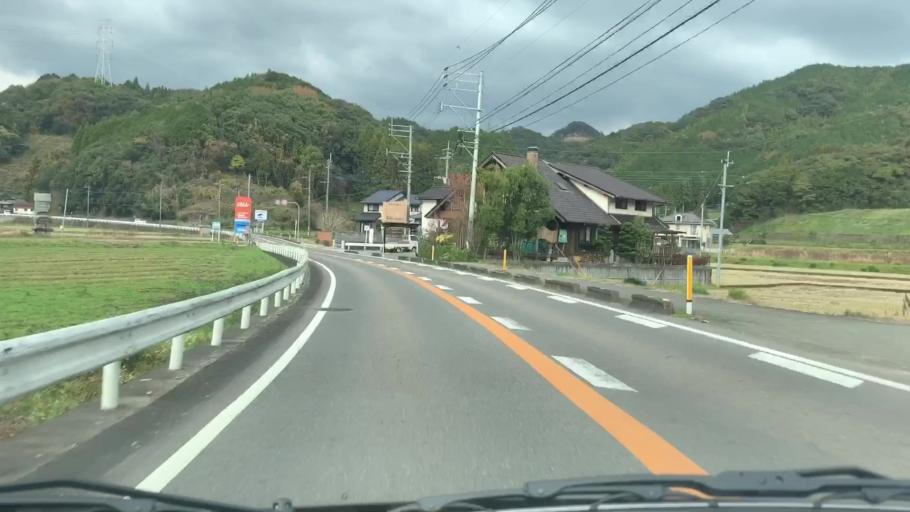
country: JP
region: Saga Prefecture
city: Ureshinomachi-shimojuku
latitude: 33.1332
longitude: 130.0303
